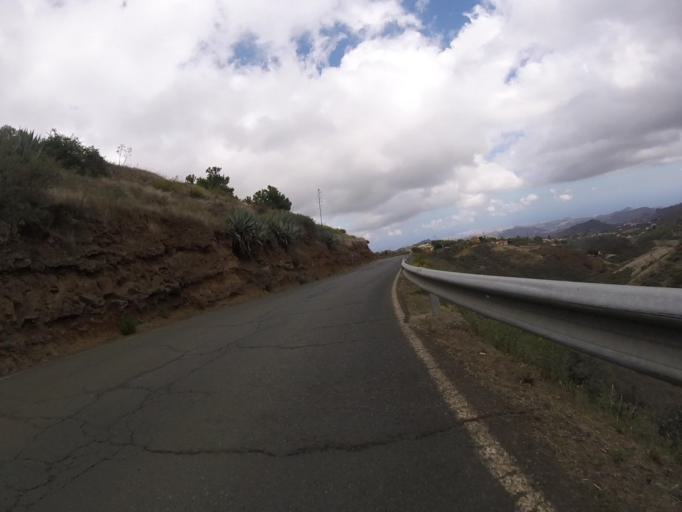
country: ES
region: Canary Islands
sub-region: Provincia de Las Palmas
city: Vega de San Mateo
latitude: 27.9969
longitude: -15.5674
